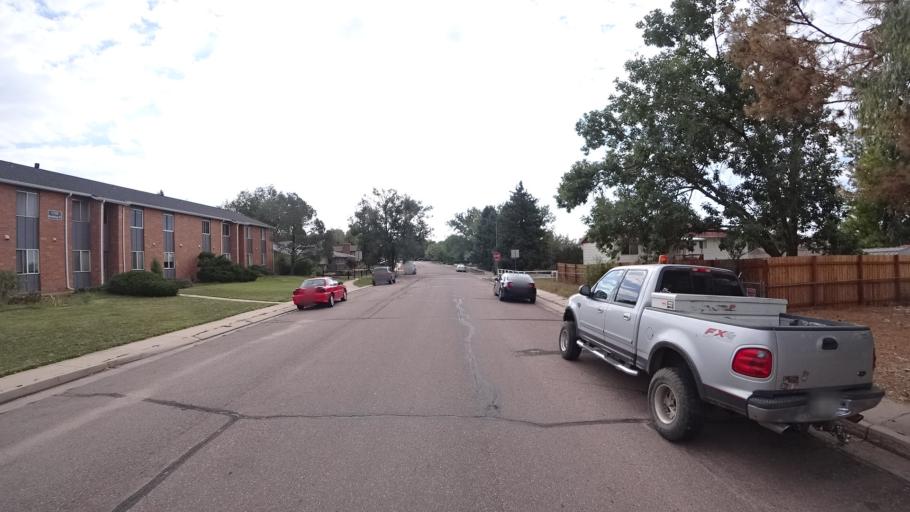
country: US
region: Colorado
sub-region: El Paso County
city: Cimarron Hills
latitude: 38.8574
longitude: -104.7455
